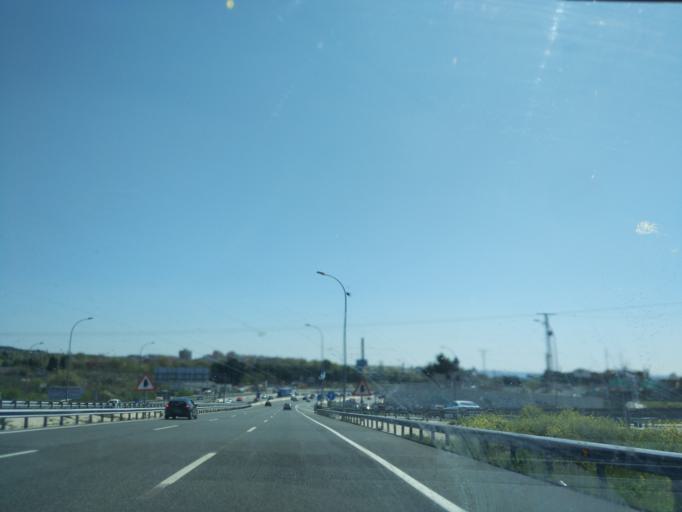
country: ES
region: Madrid
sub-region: Provincia de Madrid
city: Villa de Vallecas
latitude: 40.3585
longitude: -3.5588
